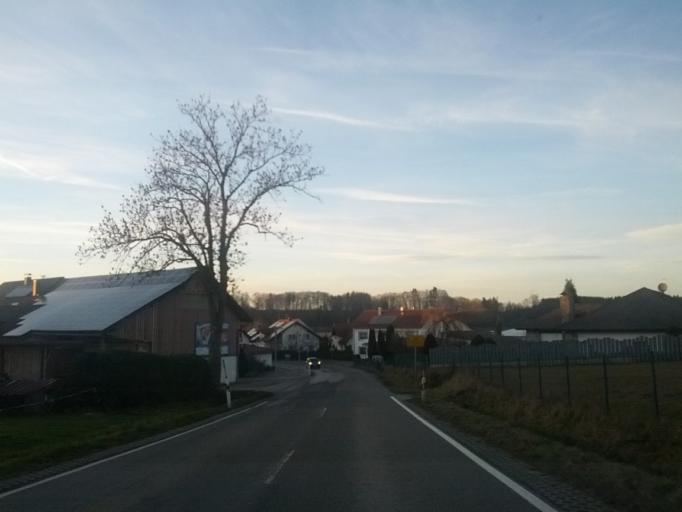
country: DE
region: Baden-Wuerttemberg
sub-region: Tuebingen Region
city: Rot an der Rot
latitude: 48.0264
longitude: 10.0454
